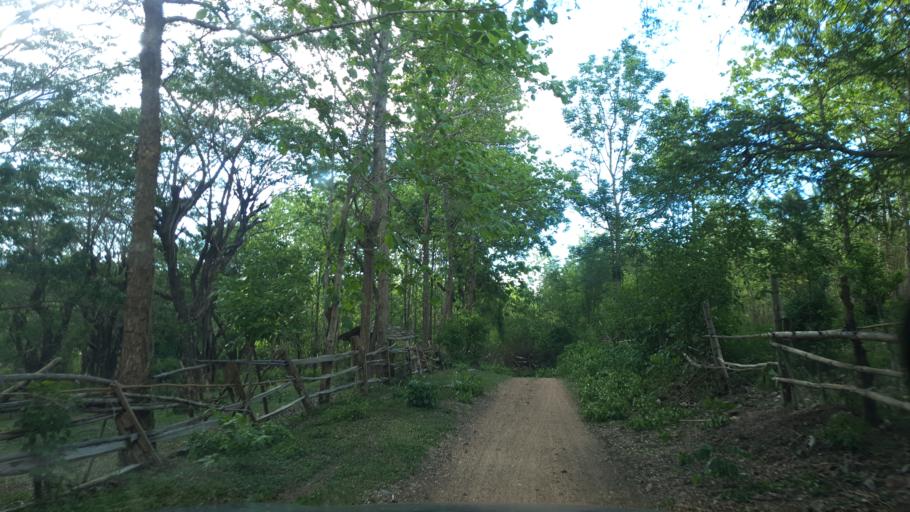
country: TH
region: Lampang
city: Sop Prap
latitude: 17.8827
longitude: 99.2927
